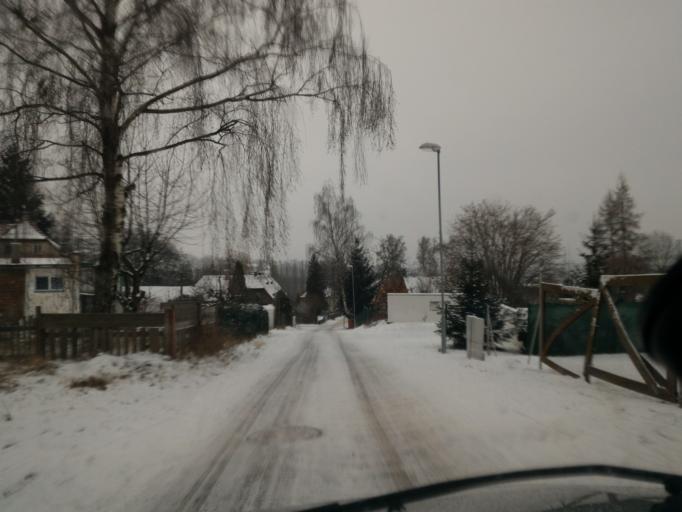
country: CZ
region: Ustecky
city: Varnsdorf
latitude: 50.9229
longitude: 14.6171
